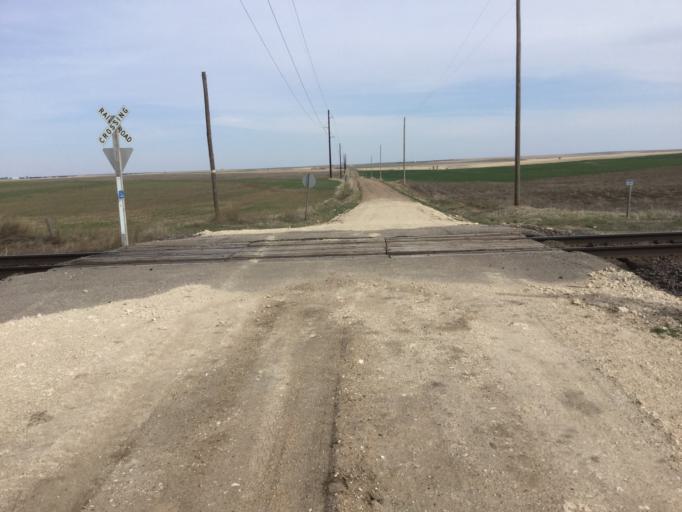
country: US
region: Kansas
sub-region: Trego County
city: WaKeeney
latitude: 38.9918
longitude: -99.7607
